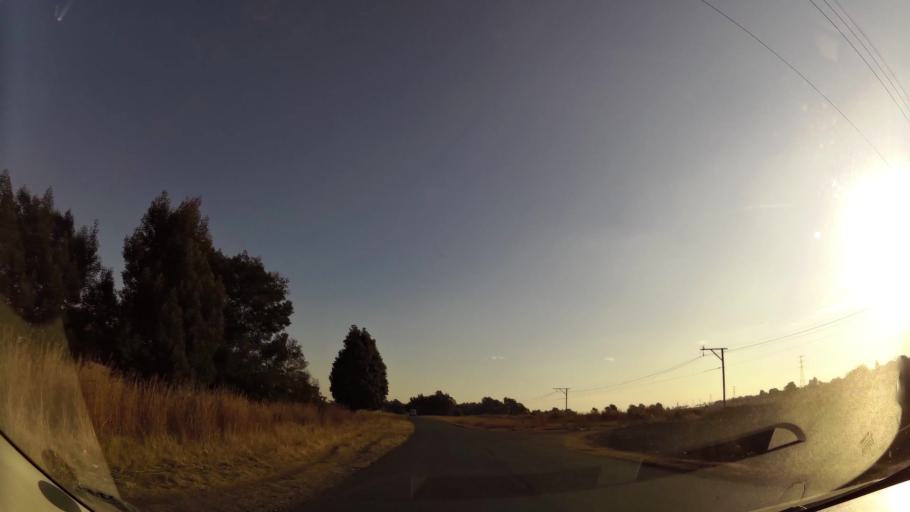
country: ZA
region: Gauteng
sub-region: West Rand District Municipality
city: Randfontein
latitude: -26.1926
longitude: 27.6847
